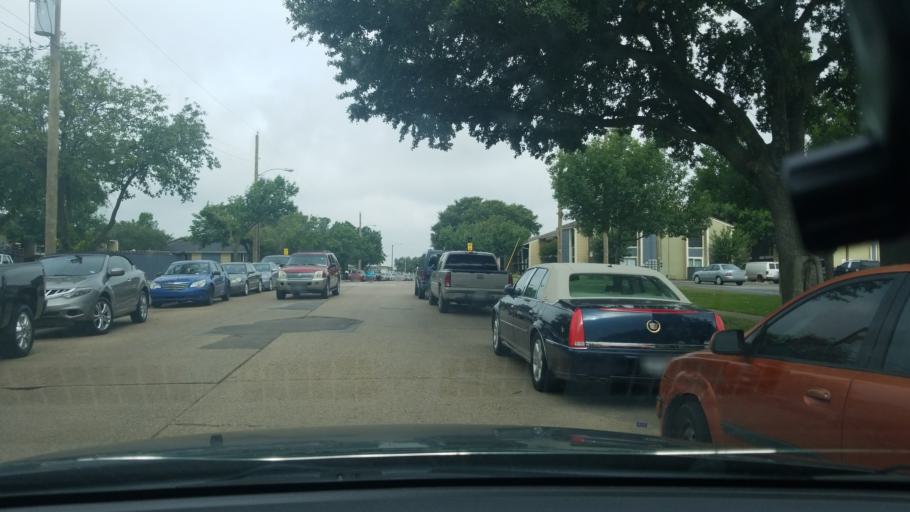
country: US
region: Texas
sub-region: Dallas County
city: Balch Springs
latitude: 32.7820
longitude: -96.6848
